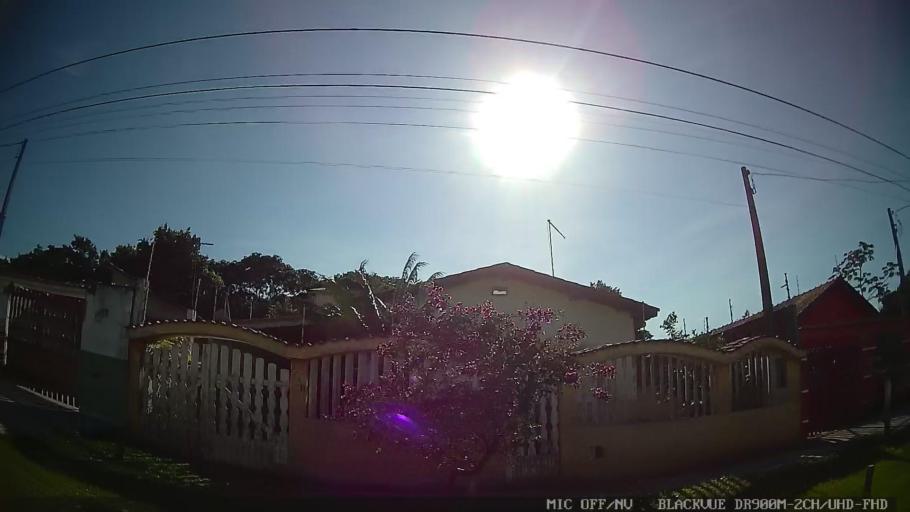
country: BR
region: Sao Paulo
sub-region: Itanhaem
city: Itanhaem
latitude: -24.2213
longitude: -46.8779
